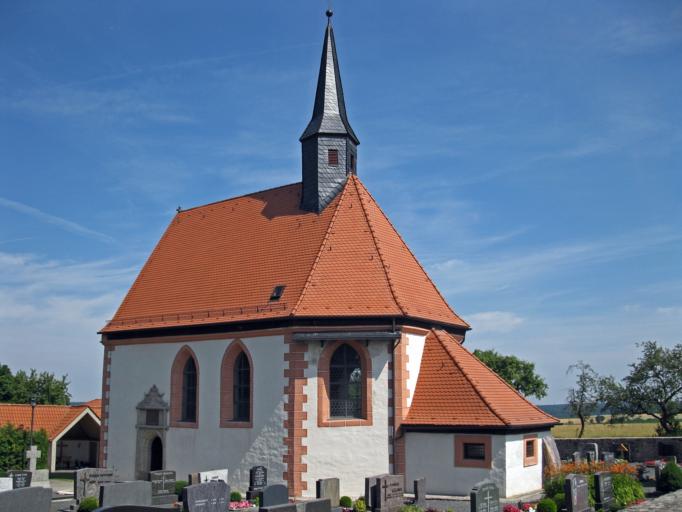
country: DE
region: Bavaria
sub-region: Regierungsbezirk Unterfranken
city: Geiselwind
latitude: 49.8260
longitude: 10.4856
